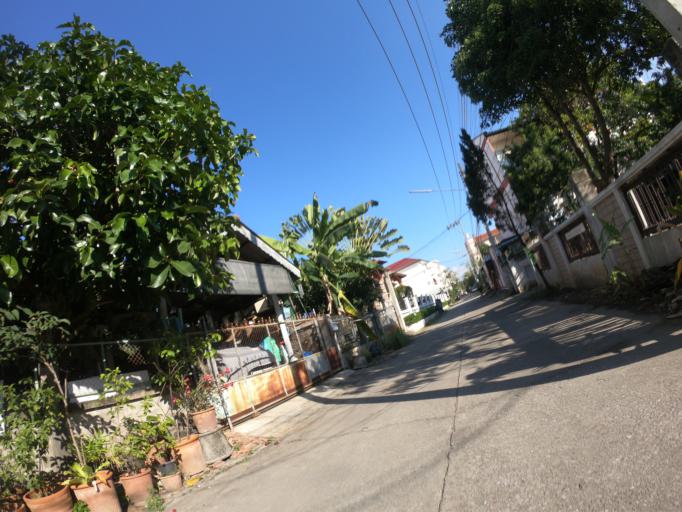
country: TH
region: Chiang Mai
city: Chiang Mai
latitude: 18.7623
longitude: 98.9782
